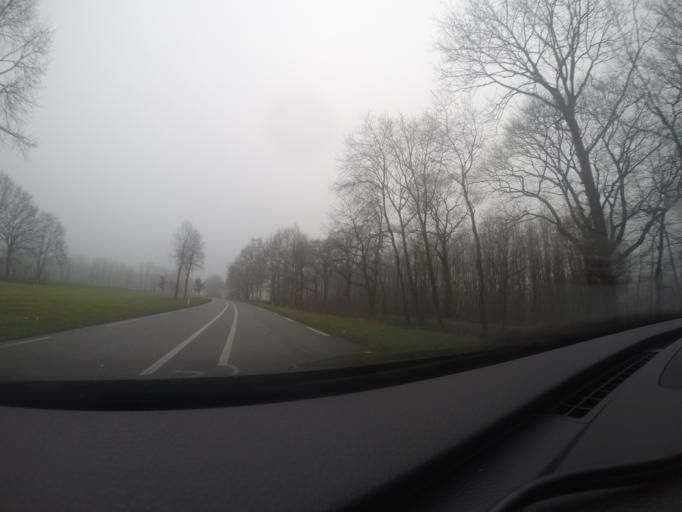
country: NL
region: Gelderland
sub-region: Gemeente Aalten
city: Aalten
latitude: 51.9089
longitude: 6.5860
